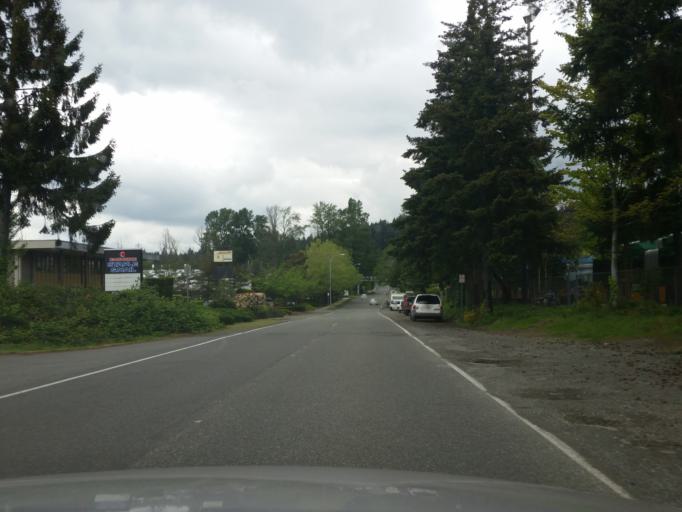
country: US
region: Washington
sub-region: King County
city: Bellevue
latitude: 47.6271
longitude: -122.1804
